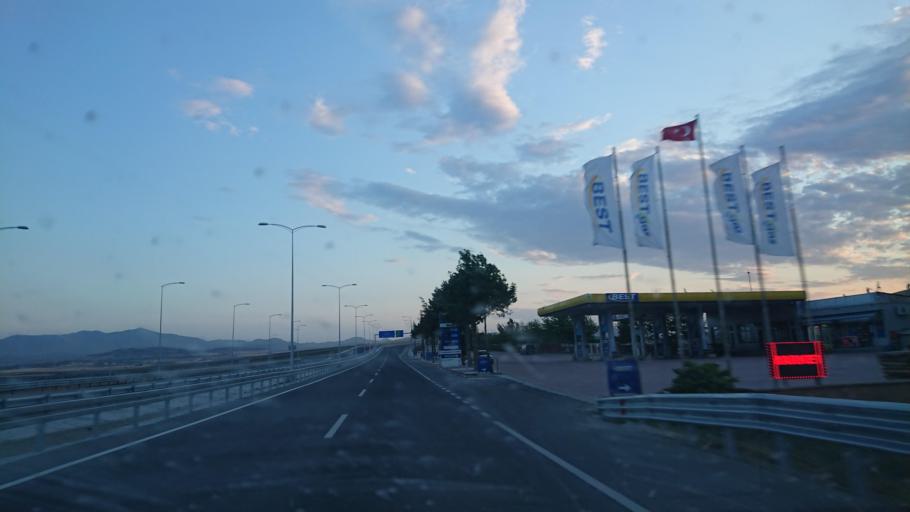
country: TR
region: Aksaray
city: Balci
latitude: 38.7758
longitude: 34.1100
